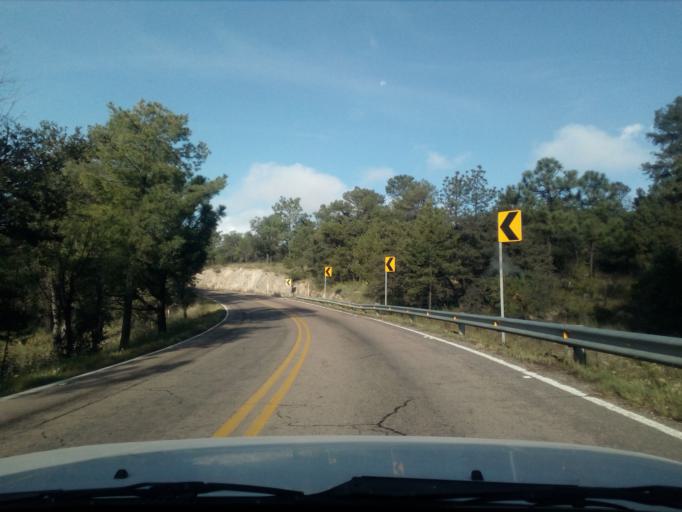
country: MX
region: Durango
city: Victoria de Durango
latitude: 23.9330
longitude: -104.9135
